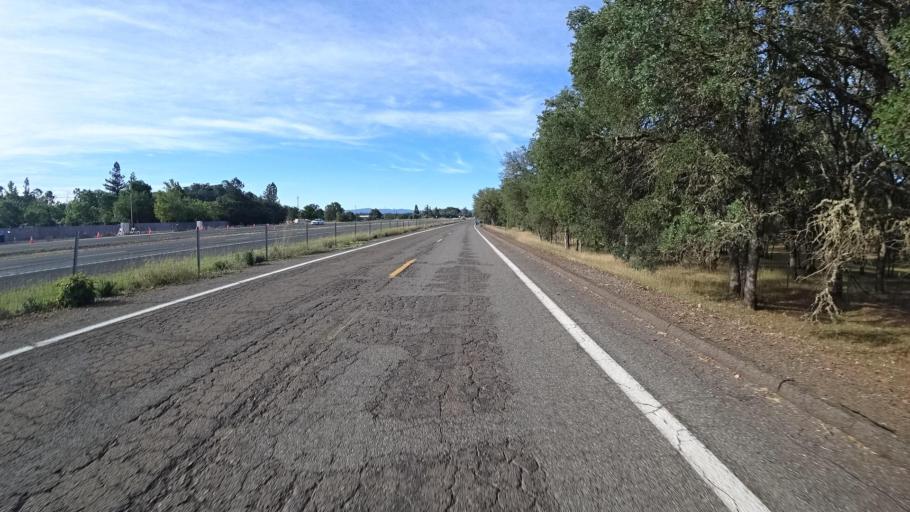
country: US
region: California
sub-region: Lake County
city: North Lakeport
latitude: 39.0761
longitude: -122.9313
